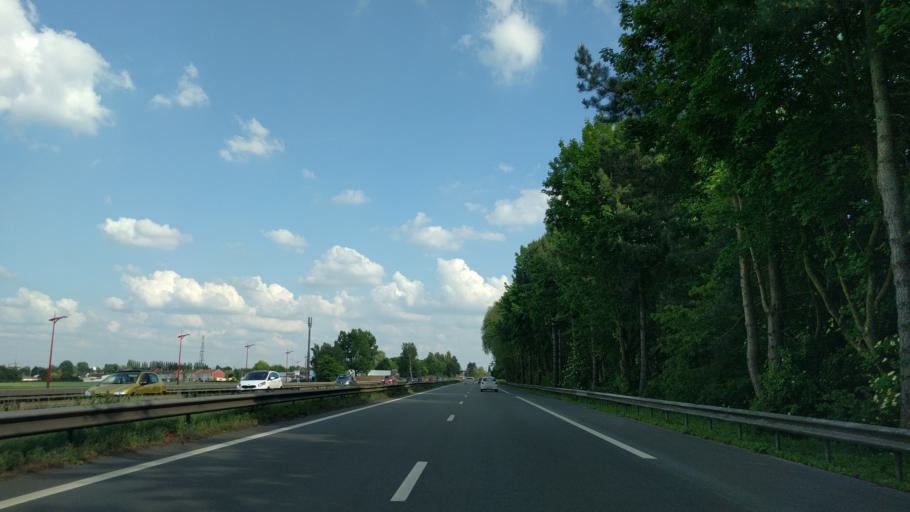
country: FR
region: Nord-Pas-de-Calais
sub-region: Departement du Nord
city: Petite-Foret
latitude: 50.3729
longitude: 3.4773
